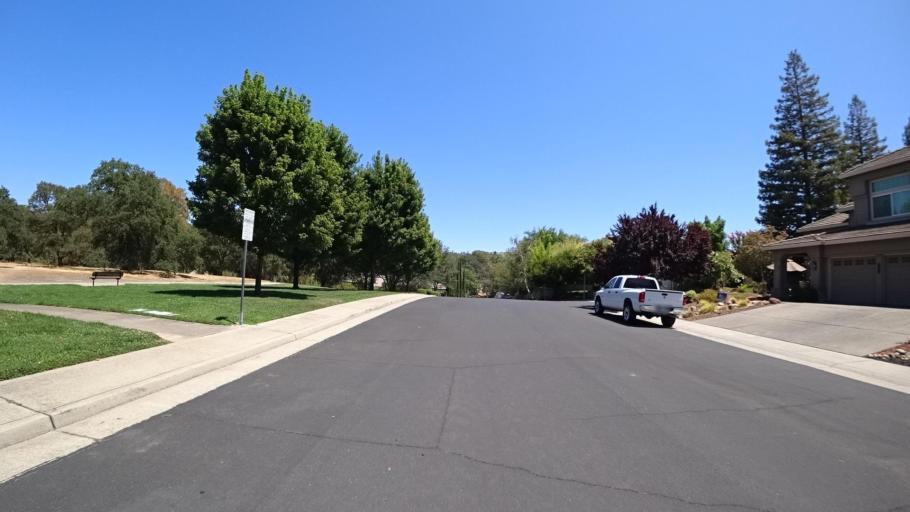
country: US
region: California
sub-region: Placer County
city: Rocklin
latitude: 38.8240
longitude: -121.2466
